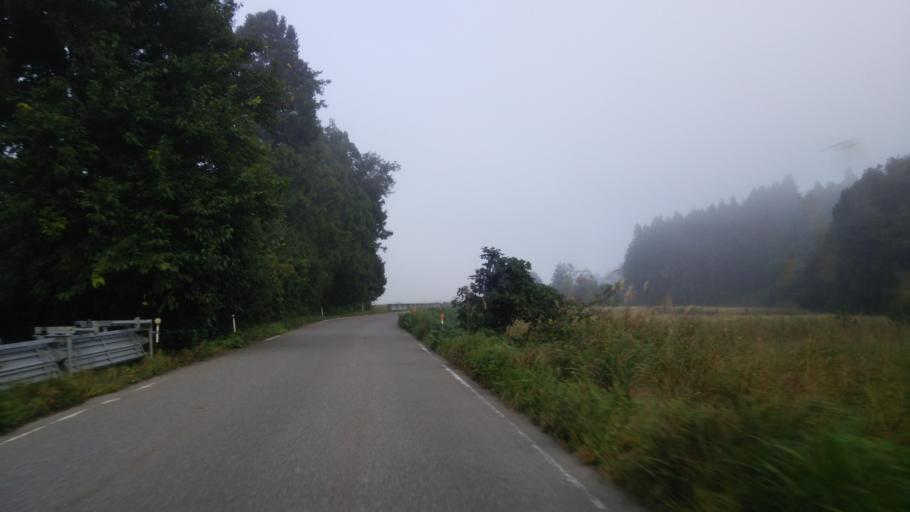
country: JP
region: Fukushima
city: Kitakata
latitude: 37.5859
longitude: 139.7746
